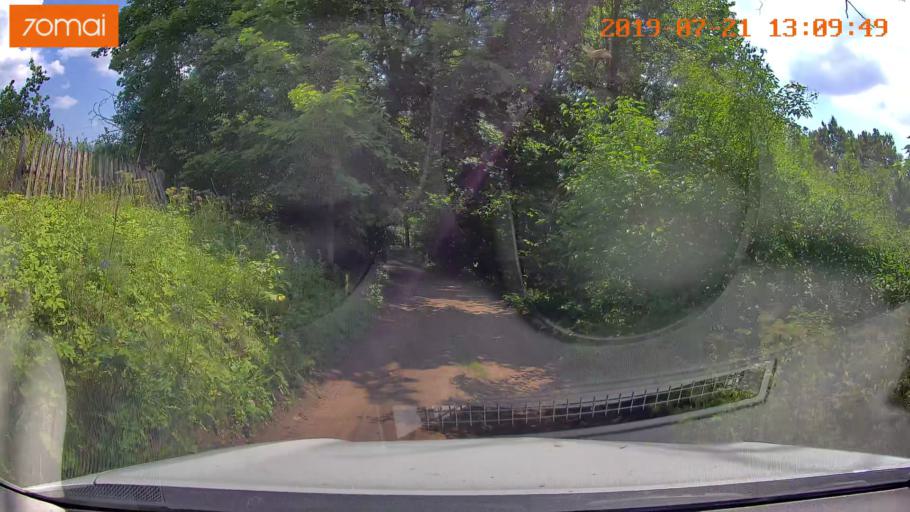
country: BY
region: Grodnenskaya
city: Lyubcha
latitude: 53.8254
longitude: 26.0470
